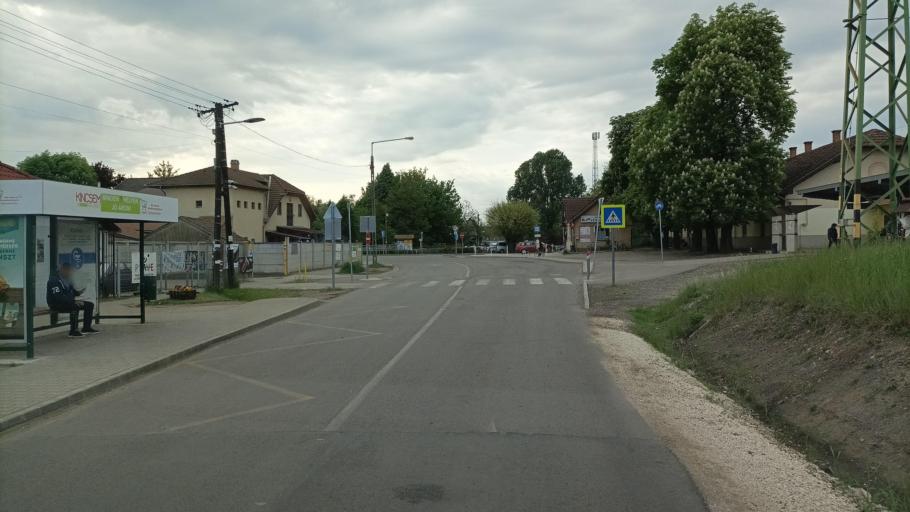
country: HU
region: Pest
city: Pilis
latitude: 47.2800
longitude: 19.5370
